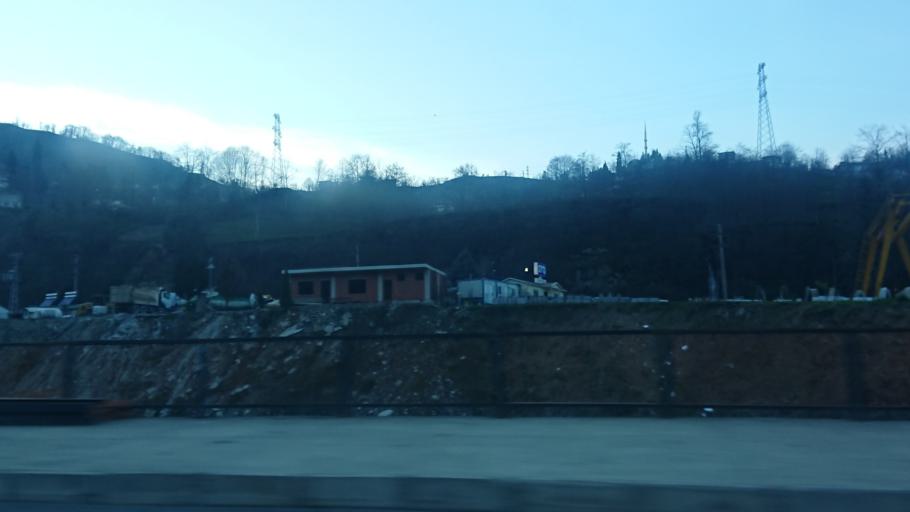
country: TR
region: Rize
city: Gundogdu
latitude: 41.0252
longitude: 40.5800
